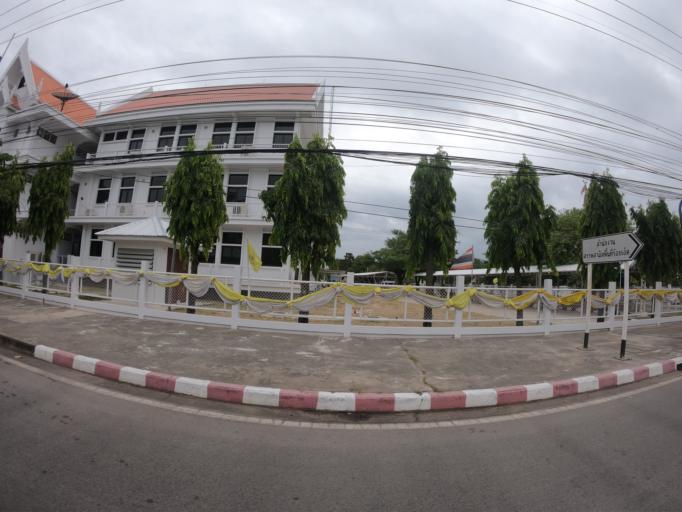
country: TH
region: Roi Et
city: Roi Et
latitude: 16.0526
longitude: 103.6532
